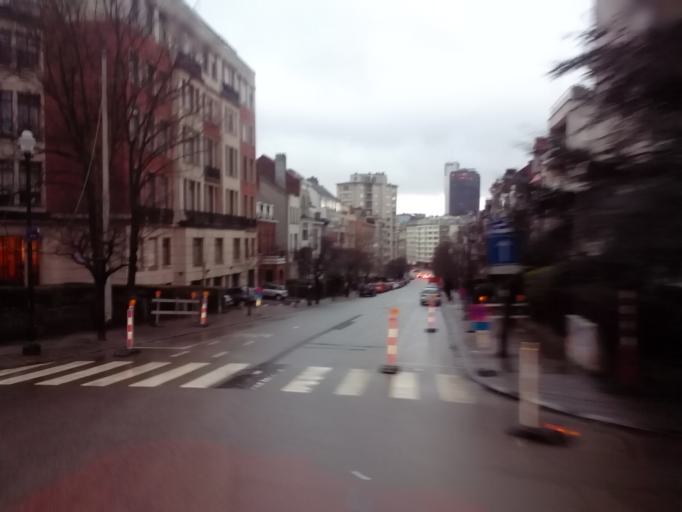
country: BE
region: Brussels Capital
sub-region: Bruxelles-Capitale
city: Brussels
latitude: 50.8163
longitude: 4.3825
